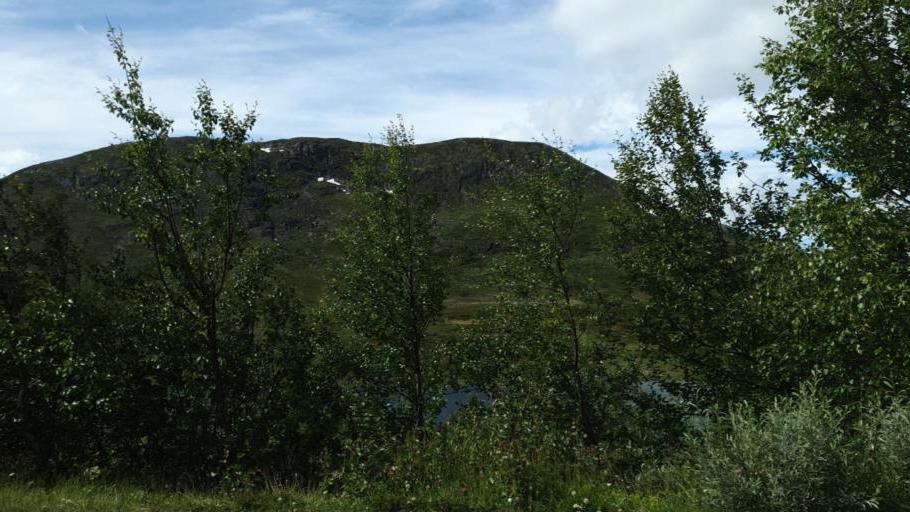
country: NO
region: Oppland
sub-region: Lom
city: Fossbergom
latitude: 61.4932
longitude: 8.8152
